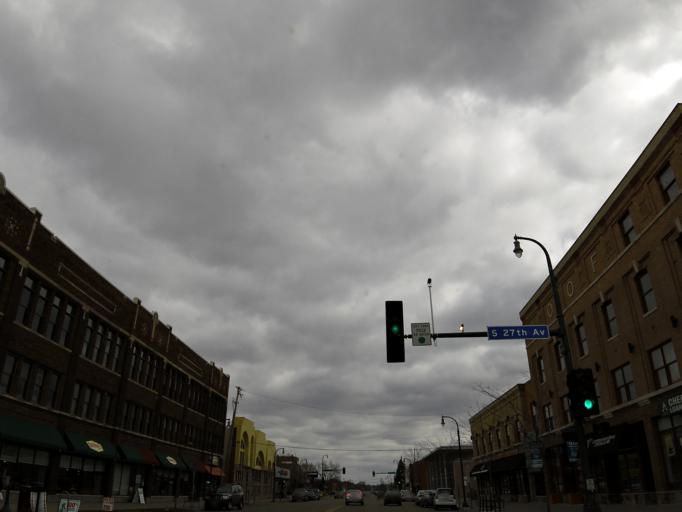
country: US
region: Minnesota
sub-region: Hennepin County
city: Minneapolis
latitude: 44.9484
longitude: -93.2333
